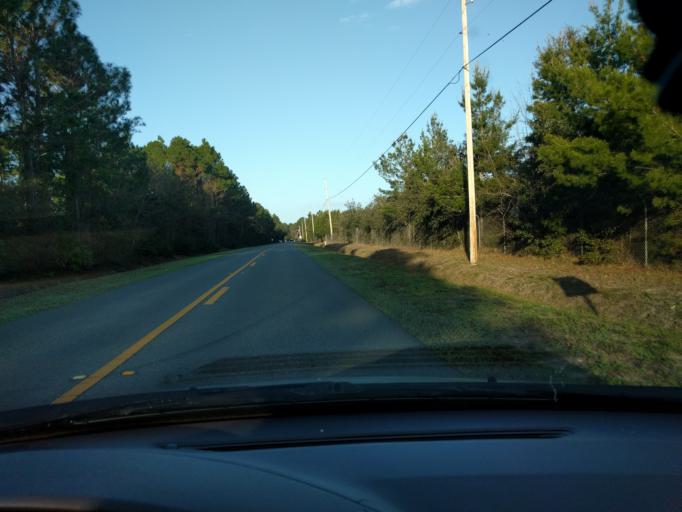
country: US
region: Florida
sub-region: Franklin County
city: Apalachicola
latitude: 29.7175
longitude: -85.0224
